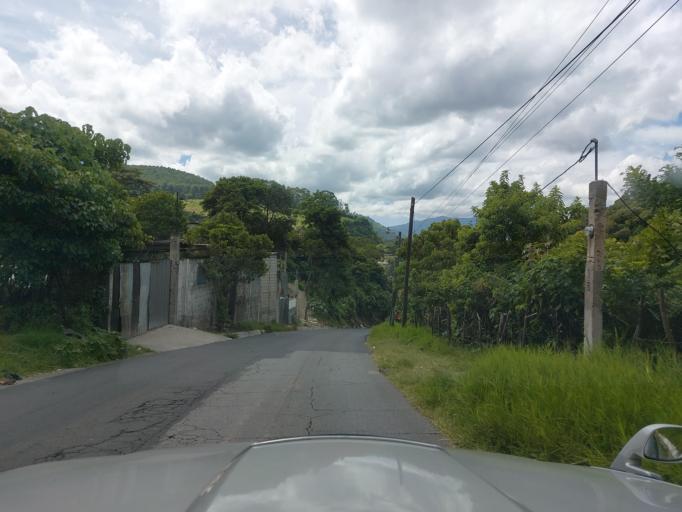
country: GT
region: Sacatepequez
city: Pastores
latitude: 14.6063
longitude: -90.7662
